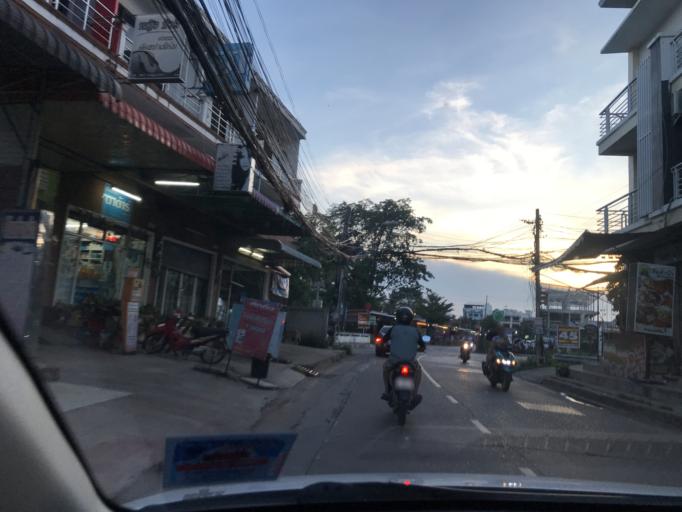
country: TH
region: Changwat Udon Thani
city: Udon Thani
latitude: 17.3959
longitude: 102.7889
